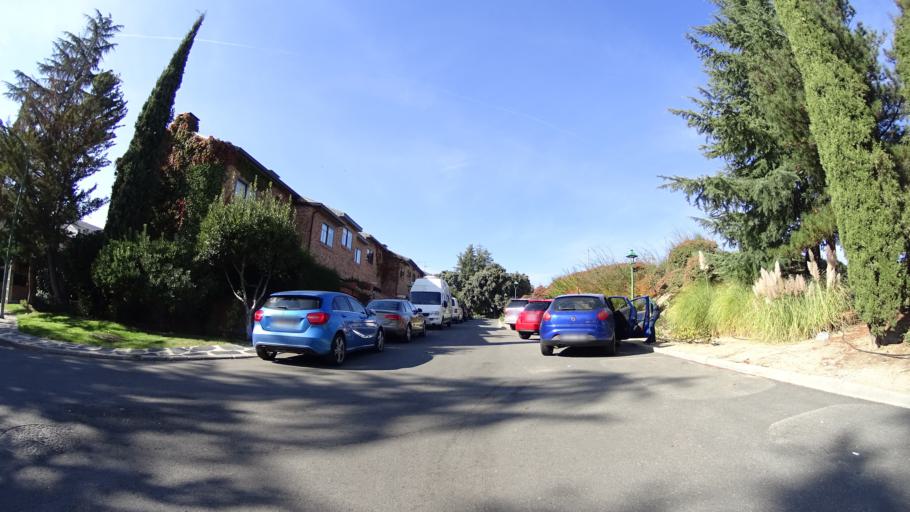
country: ES
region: Madrid
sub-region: Provincia de Madrid
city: Navalquejigo
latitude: 40.6074
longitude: -4.0287
